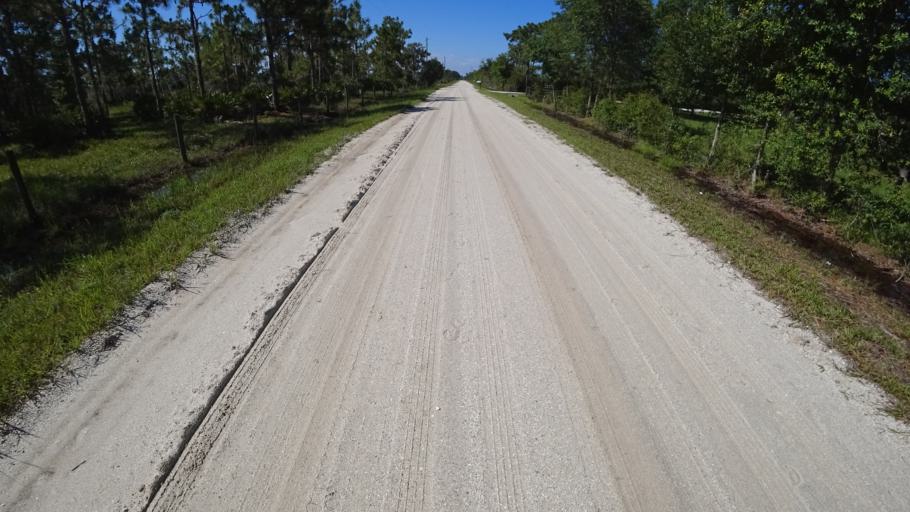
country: US
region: Florida
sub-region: Sarasota County
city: The Meadows
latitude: 27.4115
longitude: -82.2874
